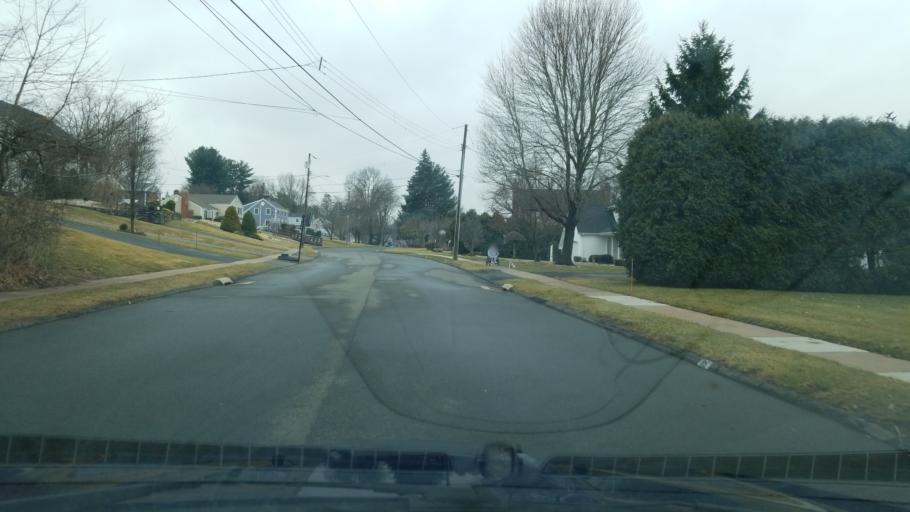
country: US
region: Connecticut
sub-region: Hartford County
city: Wethersfield
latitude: 41.6854
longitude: -72.6676
